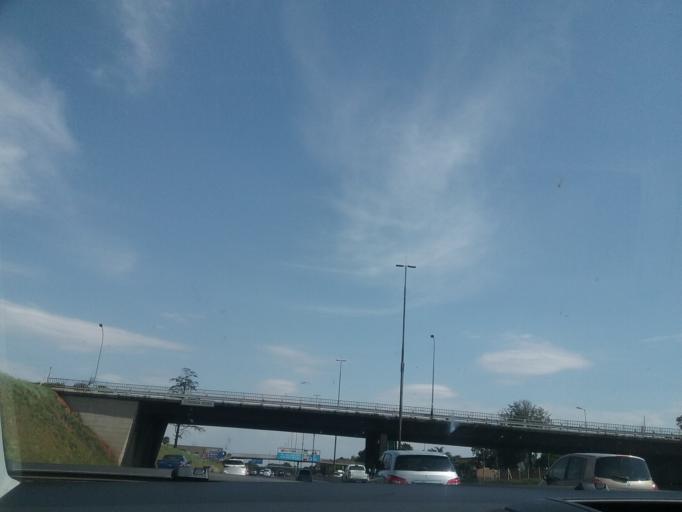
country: ZA
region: Gauteng
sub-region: Ekurhuleni Metropolitan Municipality
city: Germiston
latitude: -26.1965
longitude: 28.1322
